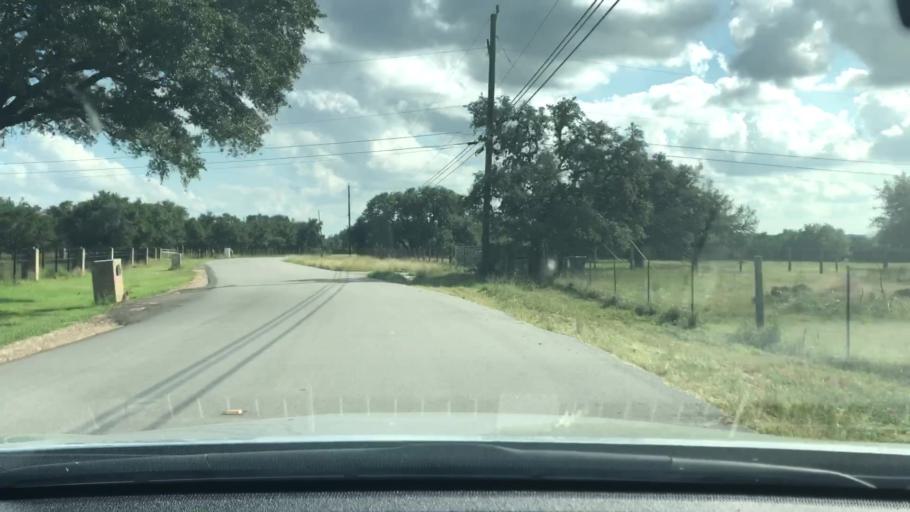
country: US
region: Texas
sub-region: Bexar County
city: Fair Oaks Ranch
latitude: 29.7593
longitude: -98.6259
